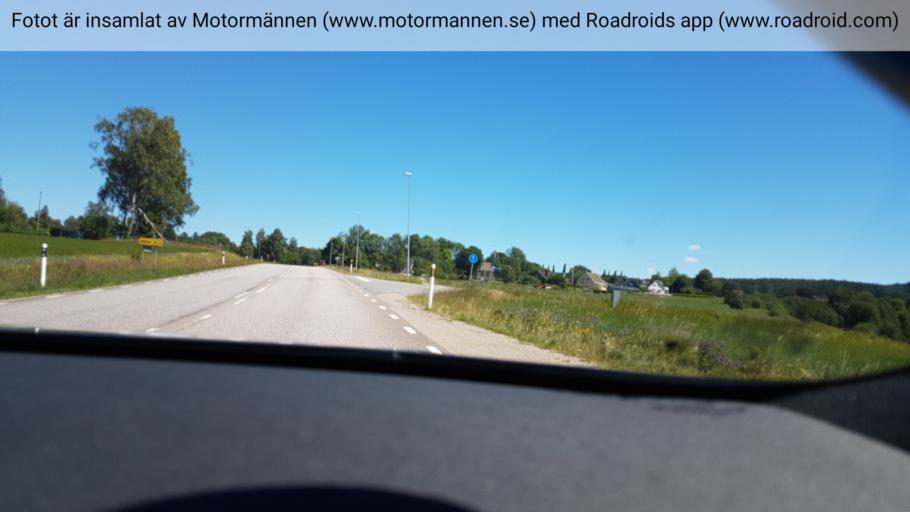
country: SE
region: Vaestra Goetaland
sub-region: Ulricehamns Kommun
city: Ulricehamn
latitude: 57.8955
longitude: 13.4551
